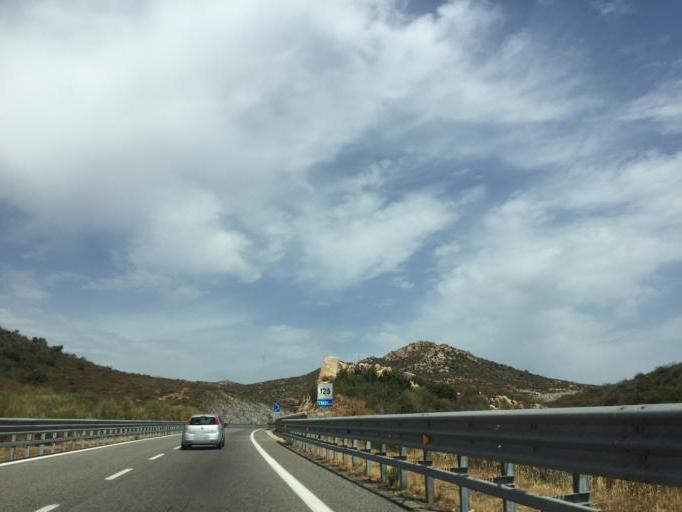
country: IT
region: Sardinia
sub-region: Provincia di Olbia-Tempio
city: San Teodoro
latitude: 40.7740
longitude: 9.6263
